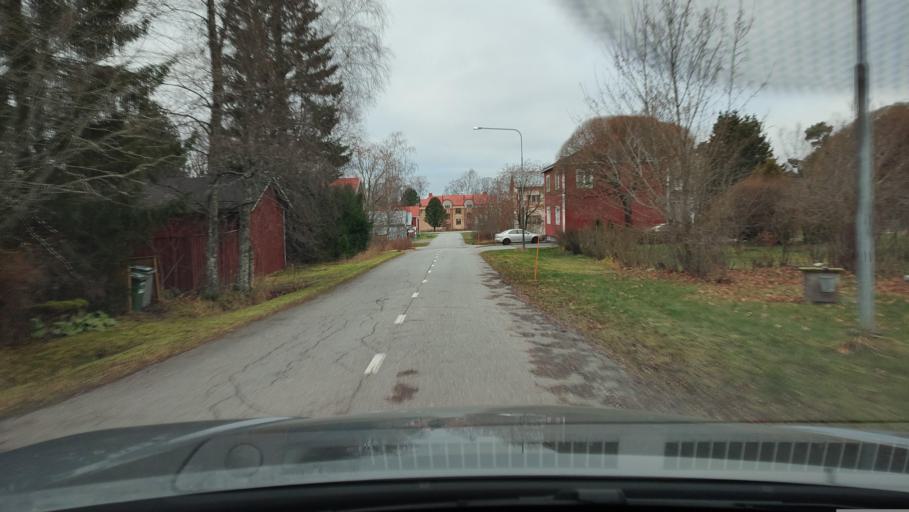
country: FI
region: Ostrobothnia
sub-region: Sydosterbotten
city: Kristinestad
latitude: 62.2683
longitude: 21.3936
